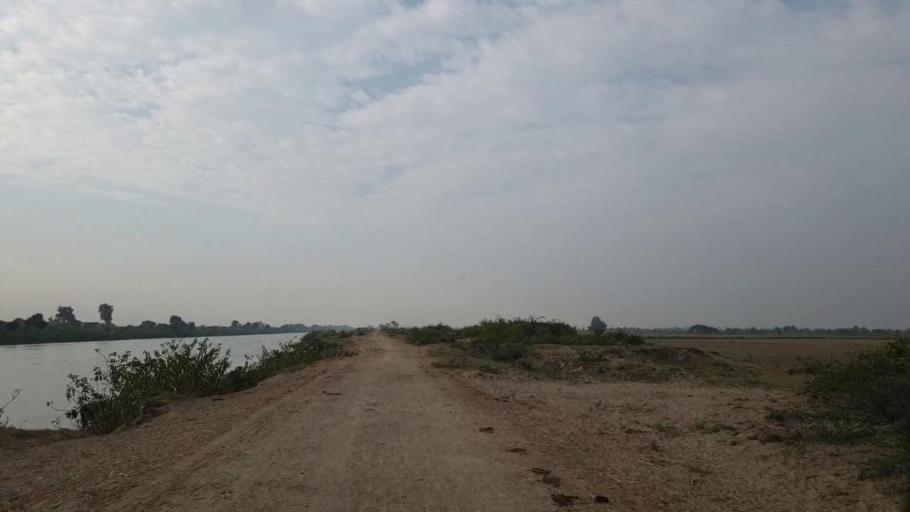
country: PK
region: Sindh
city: Tando Muhammad Khan
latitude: 25.0901
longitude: 68.4127
